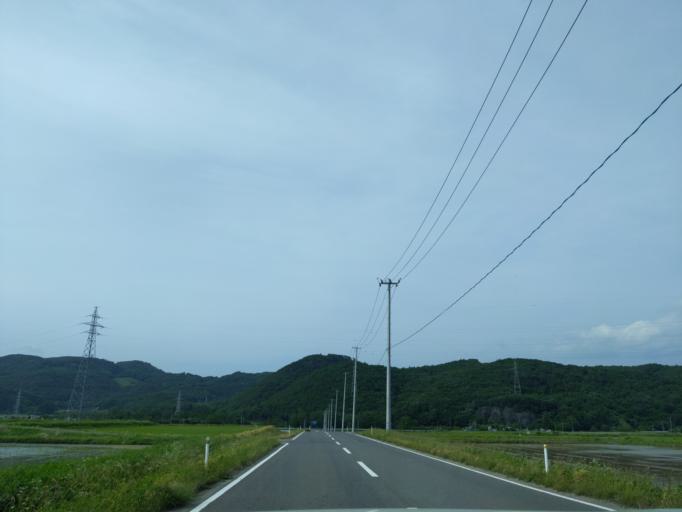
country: JP
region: Fukushima
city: Motomiya
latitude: 37.4727
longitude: 140.3162
